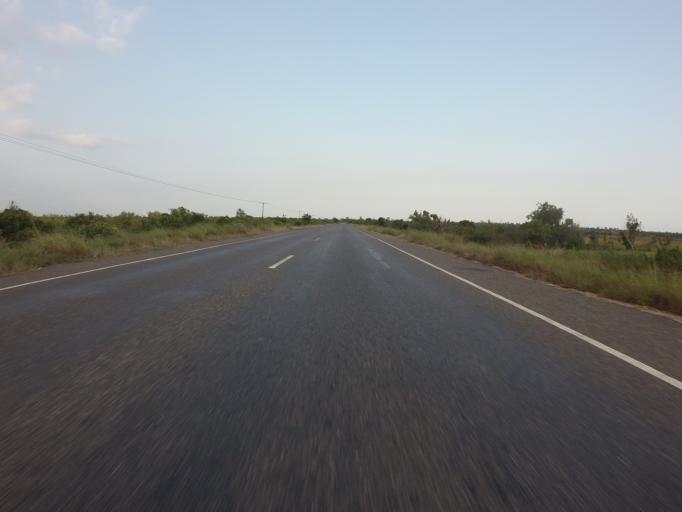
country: GH
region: Volta
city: Anloga
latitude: 6.0775
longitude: 0.5938
